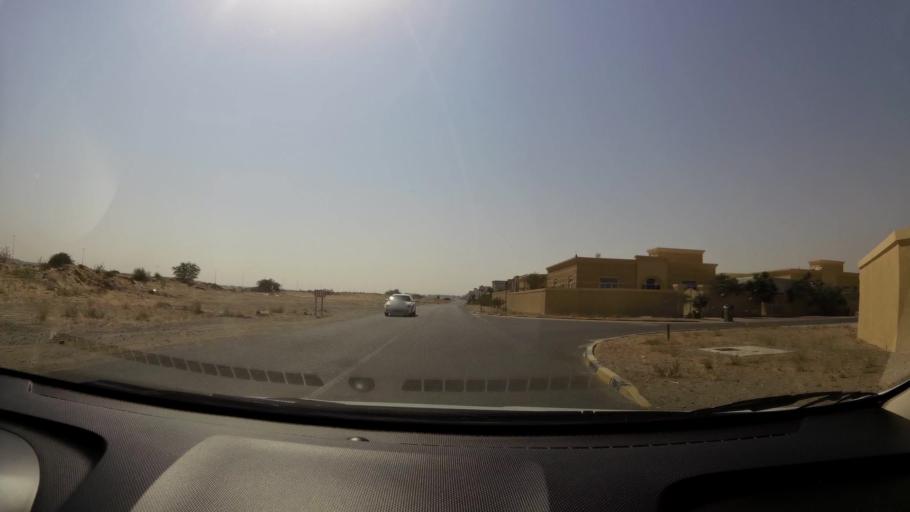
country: AE
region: Ajman
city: Ajman
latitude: 25.4165
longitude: 55.5429
